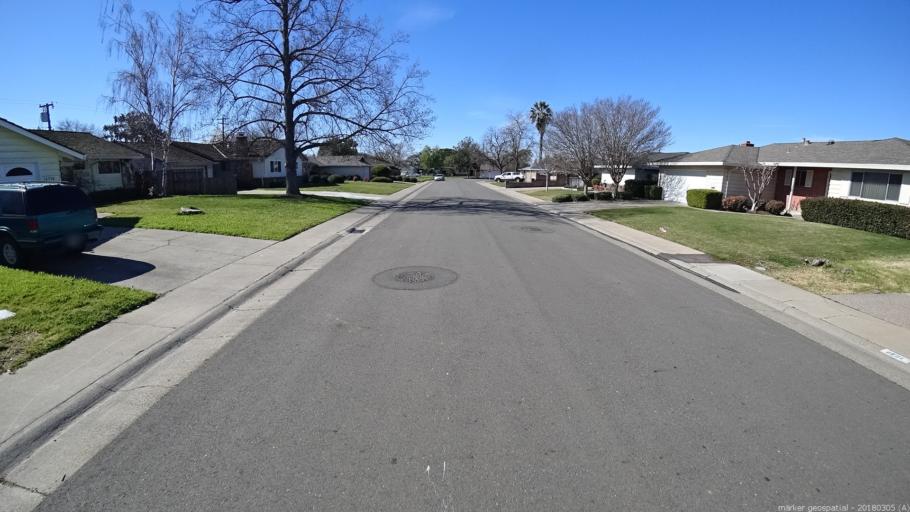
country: US
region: California
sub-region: Sacramento County
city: Florin
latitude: 38.4938
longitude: -121.4260
